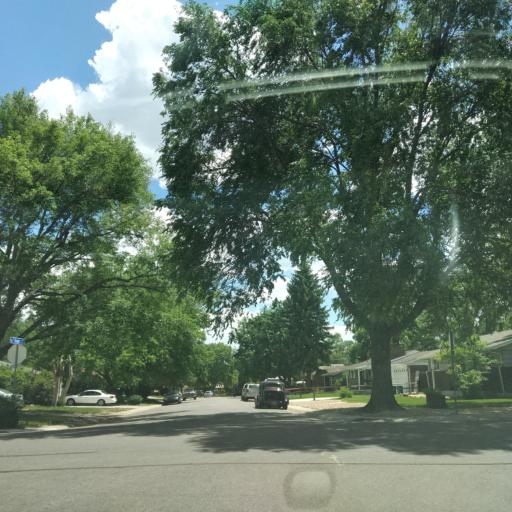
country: US
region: Colorado
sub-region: Jefferson County
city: Lakewood
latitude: 39.6859
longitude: -105.0937
